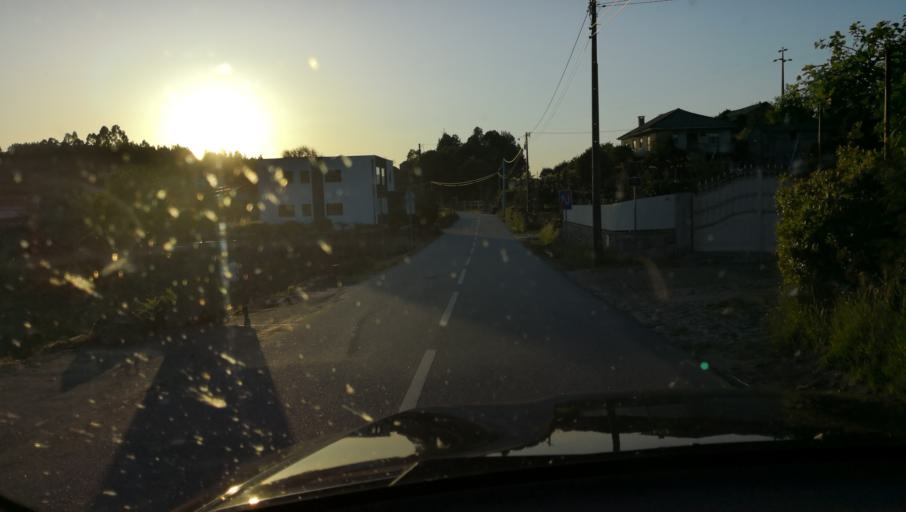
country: PT
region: Vila Real
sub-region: Mondim de Basto
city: Mondim de Basto
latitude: 41.4084
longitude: -7.9278
